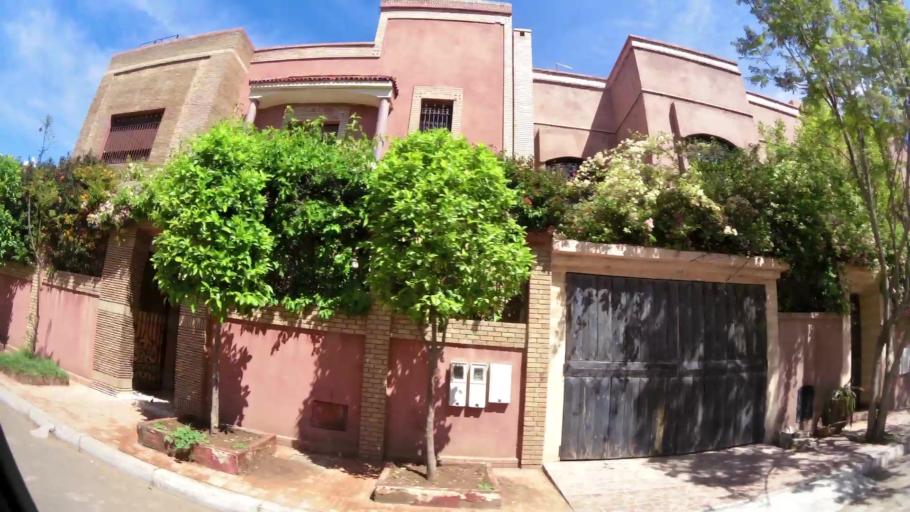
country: MA
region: Marrakech-Tensift-Al Haouz
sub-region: Marrakech
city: Marrakesh
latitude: 31.6614
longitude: -7.9911
